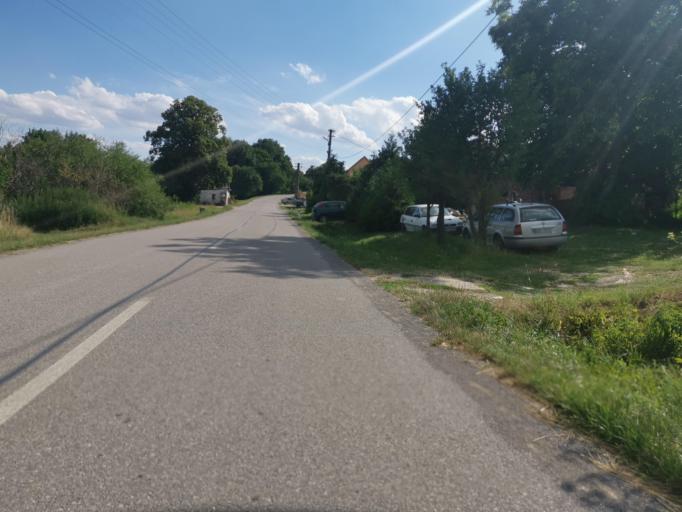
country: CZ
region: South Moravian
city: Knezdub
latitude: 48.7955
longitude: 17.4081
